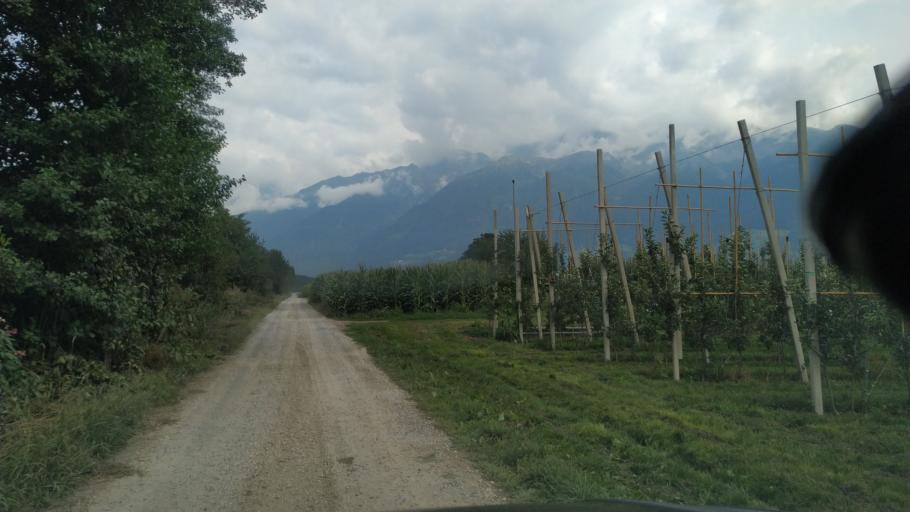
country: IT
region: Trentino-Alto Adige
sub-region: Bolzano
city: Sluderno
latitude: 46.6591
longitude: 10.5713
